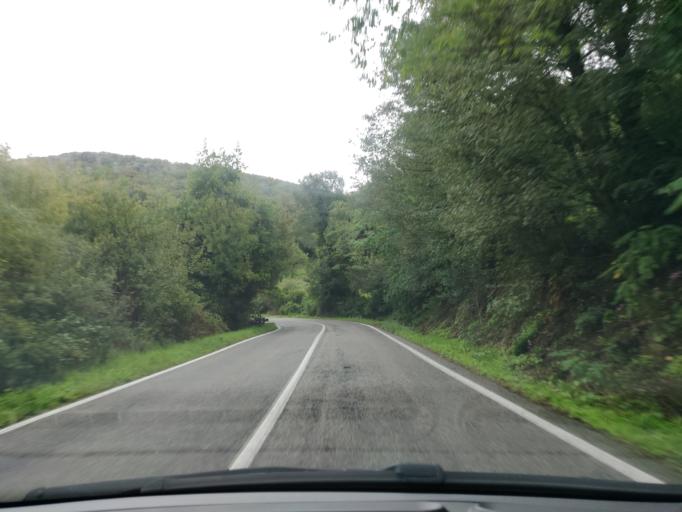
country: IT
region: Latium
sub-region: Citta metropolitana di Roma Capitale
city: Allumiere
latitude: 42.1481
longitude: 11.8978
